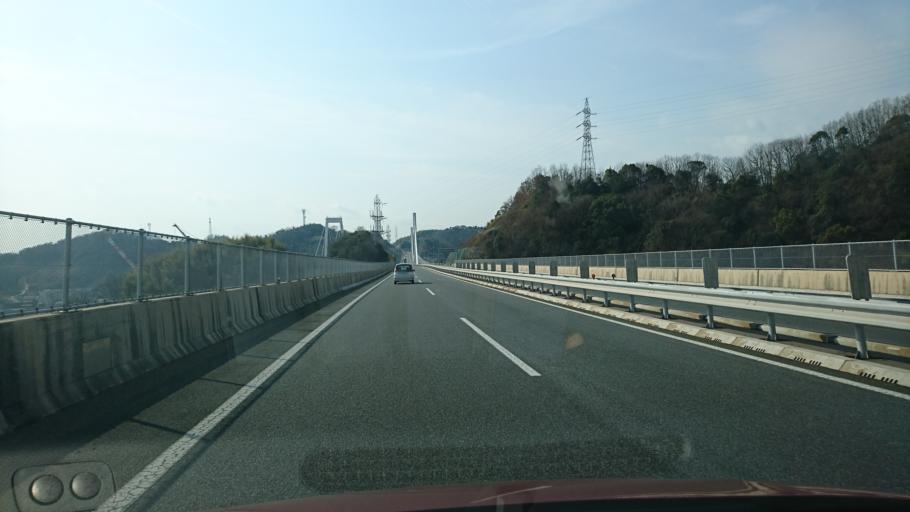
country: JP
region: Hiroshima
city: Onomichi
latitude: 34.4132
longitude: 133.2194
